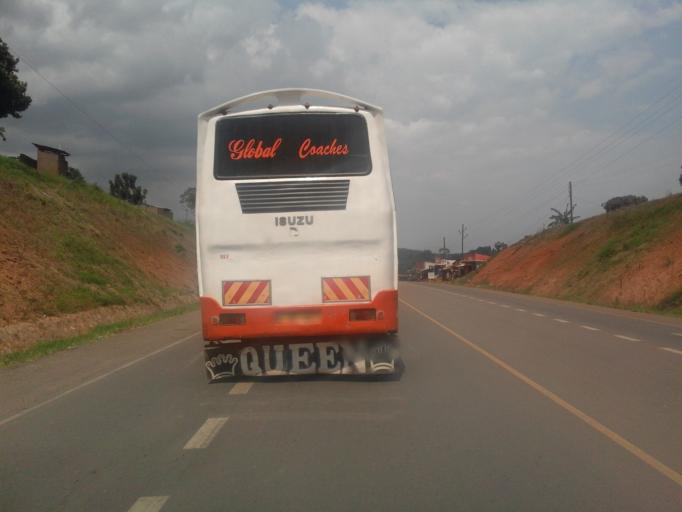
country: UG
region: Central Region
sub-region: Mpigi District
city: Mpigi
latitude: 0.2439
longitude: 32.3784
